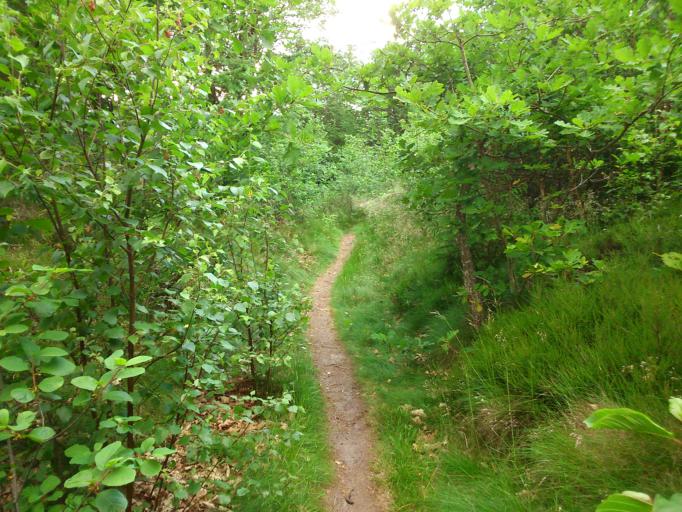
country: DK
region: Central Jutland
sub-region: Ringkobing-Skjern Kommune
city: Skjern
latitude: 55.9977
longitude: 8.4332
